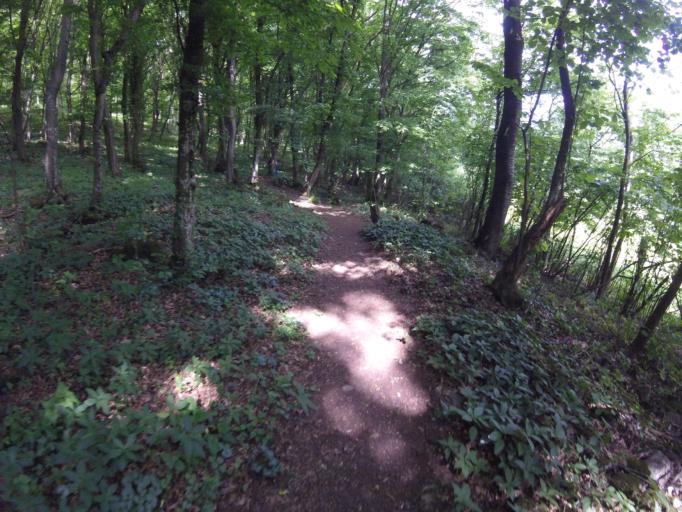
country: SK
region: Kosicky
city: Medzev
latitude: 48.6230
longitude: 20.8578
